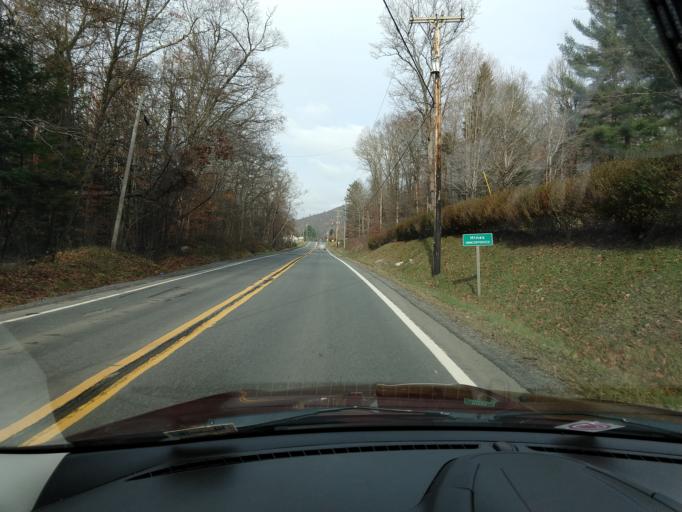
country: US
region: West Virginia
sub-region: Greenbrier County
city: Rainelle
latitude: 37.9787
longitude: -80.7120
